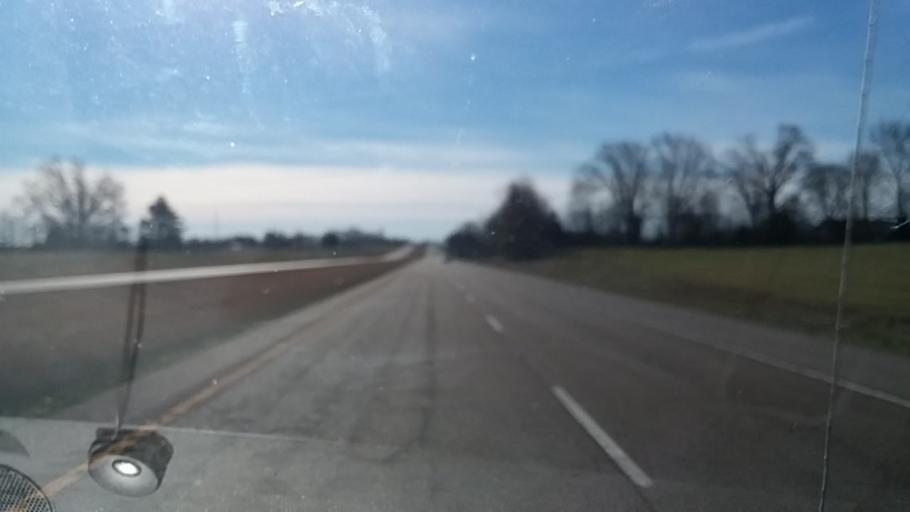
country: US
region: Tennessee
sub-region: Lauderdale County
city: Halls
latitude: 35.9444
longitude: -89.3037
